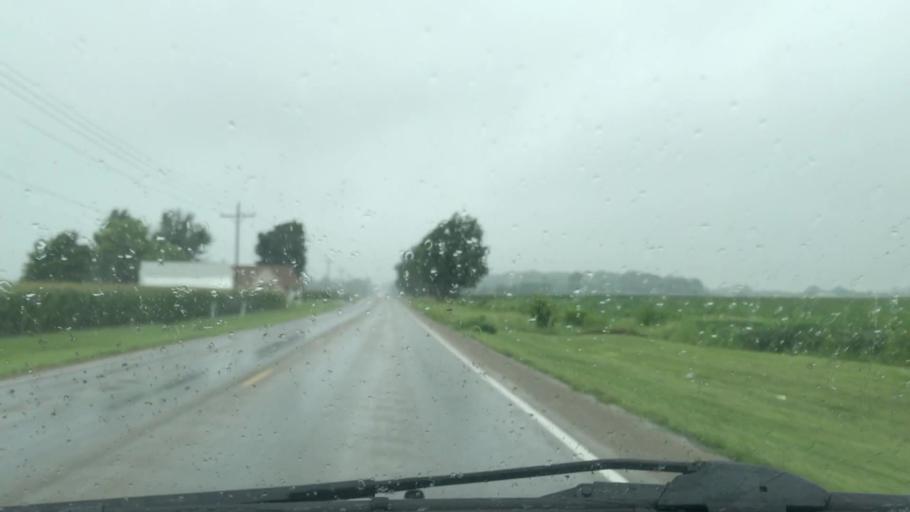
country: US
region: Indiana
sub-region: Hamilton County
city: Sheridan
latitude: 40.1186
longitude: -86.1835
